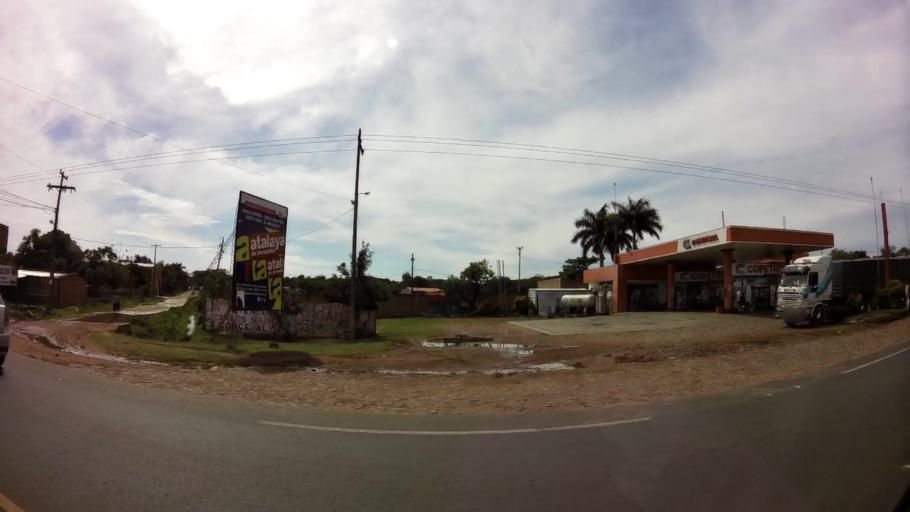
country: PY
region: Central
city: Limpio
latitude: -25.1589
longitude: -57.4746
